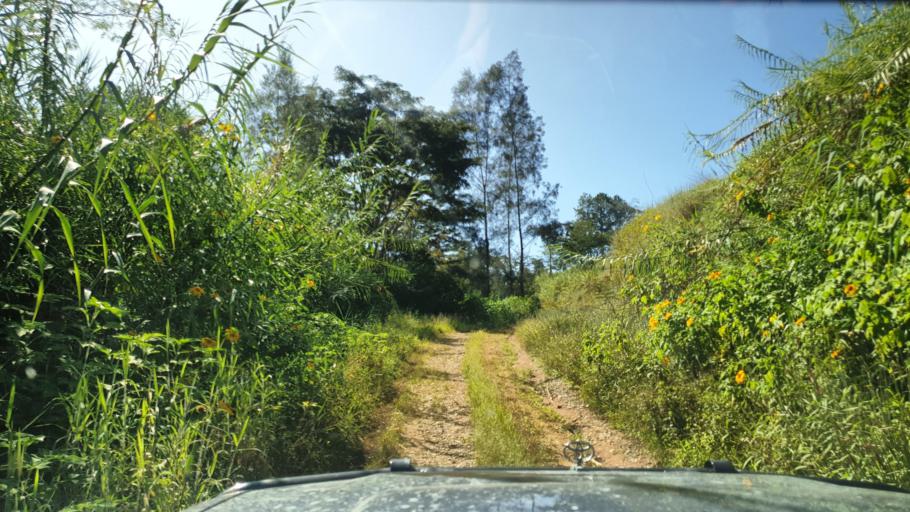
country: PG
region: Western Highlands
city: Rauna
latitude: -5.8037
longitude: 144.3710
